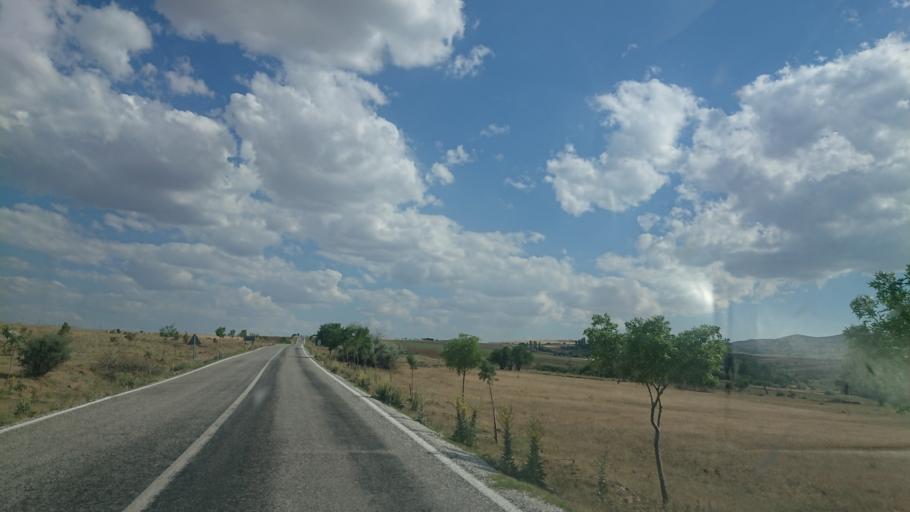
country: TR
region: Aksaray
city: Sariyahsi
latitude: 38.9573
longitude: 33.8379
